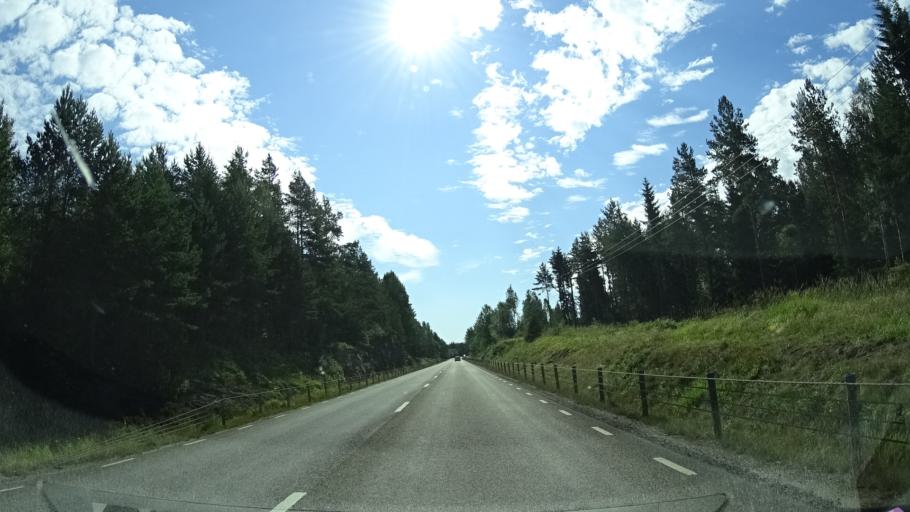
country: SE
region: Vaermland
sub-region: Arjangs Kommun
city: Arjaeng
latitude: 59.4486
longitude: 12.0628
